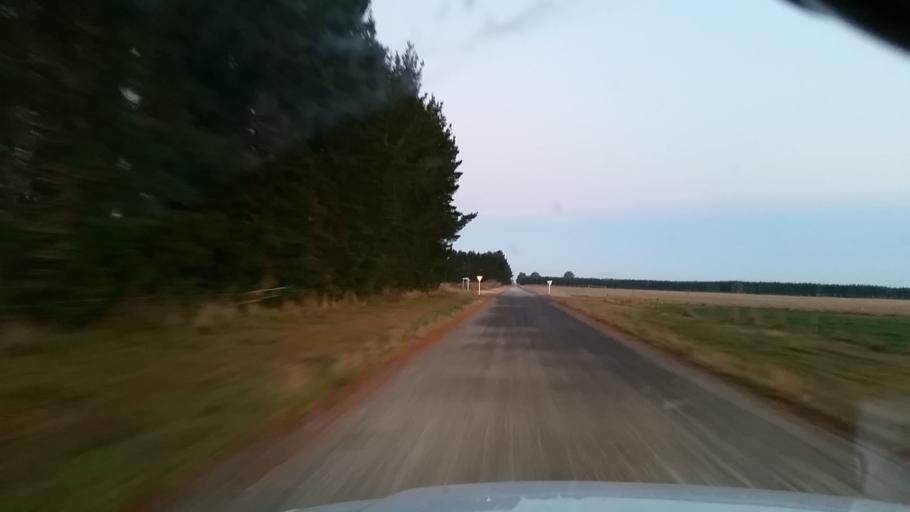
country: NZ
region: Canterbury
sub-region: Ashburton District
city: Tinwald
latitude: -43.9578
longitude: 171.6234
